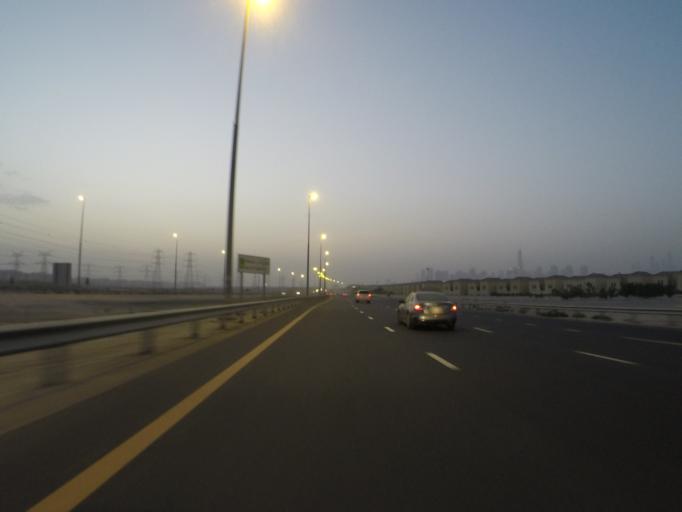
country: AE
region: Dubai
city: Dubai
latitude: 25.0413
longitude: 55.1557
